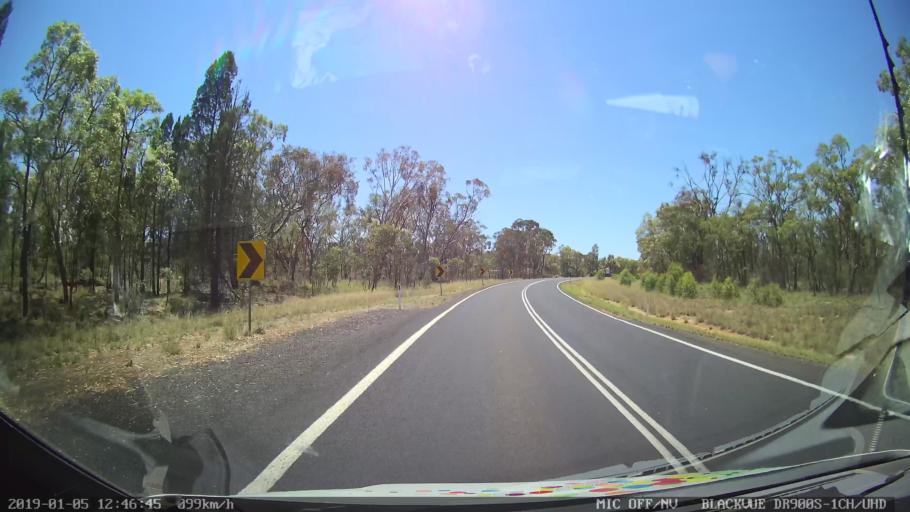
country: AU
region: New South Wales
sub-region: Warrumbungle Shire
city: Coonabarabran
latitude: -31.1148
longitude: 149.5669
